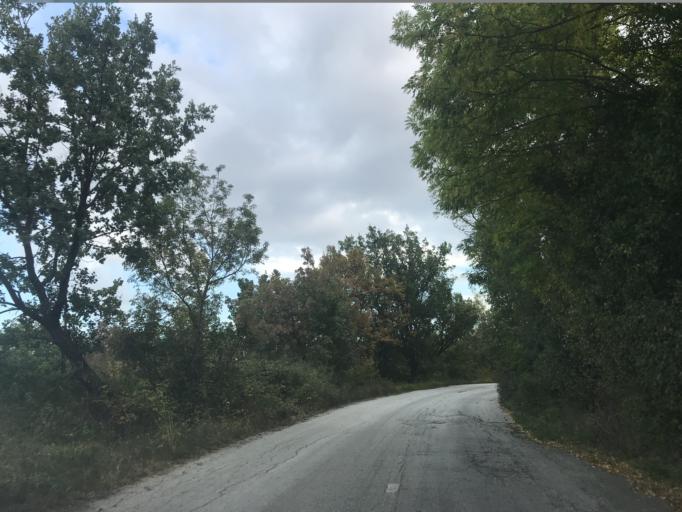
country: IT
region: Molise
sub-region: Provincia di Campobasso
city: Duronia
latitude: 41.6791
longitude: 14.4530
